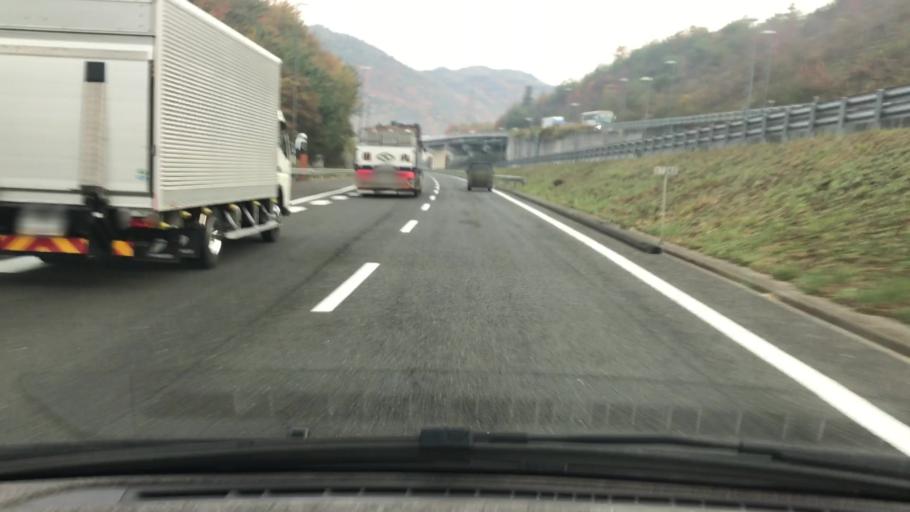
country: JP
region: Hyogo
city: Sandacho
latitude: 34.7917
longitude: 135.2248
